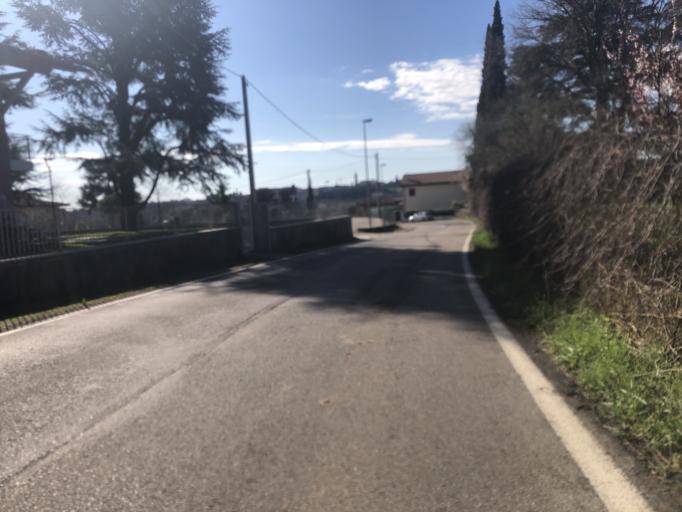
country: IT
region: Veneto
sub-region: Provincia di Verona
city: Ospedaletto
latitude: 45.4866
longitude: 10.8459
